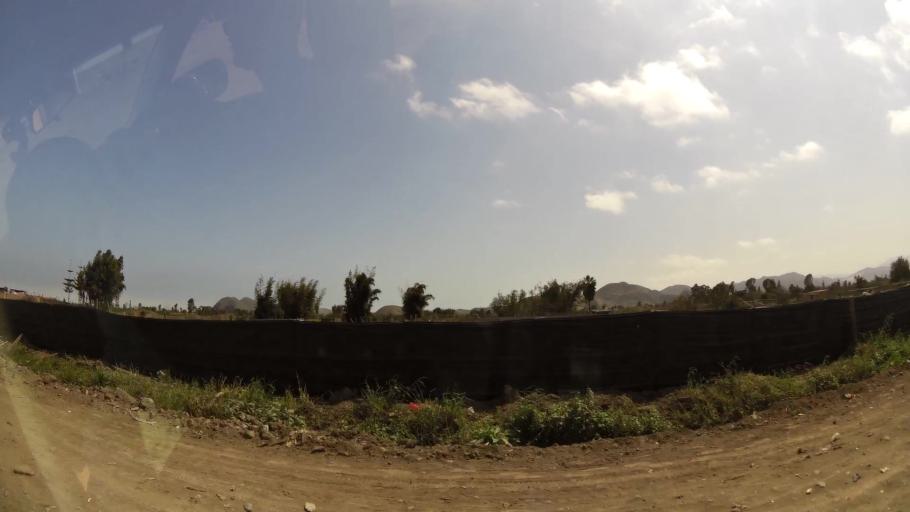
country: PE
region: Lima
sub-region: Provincia de Canete
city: Mala
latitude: -12.6711
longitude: -76.6454
